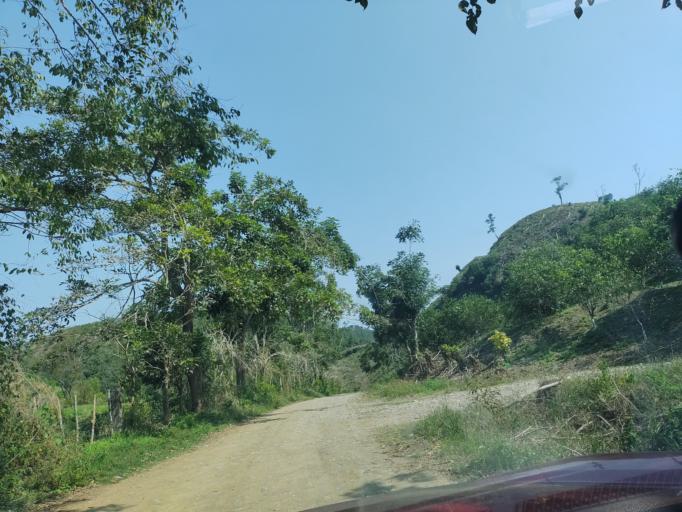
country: MX
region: Veracruz
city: Agua Dulce
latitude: 20.3368
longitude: -97.1975
